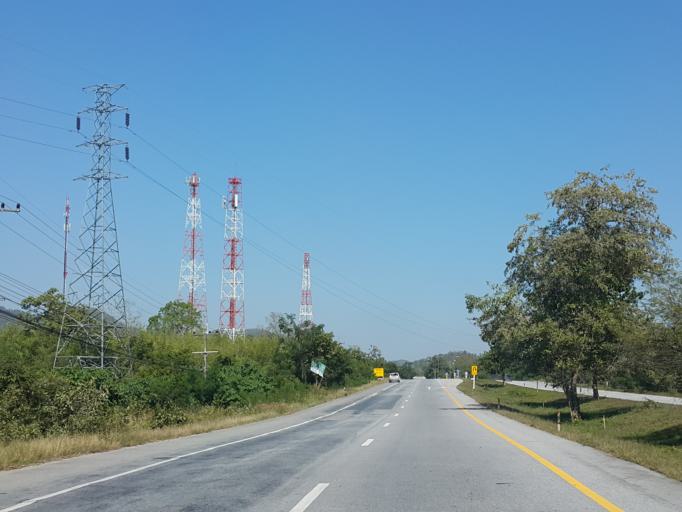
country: TH
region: Lampang
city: Sop Prap
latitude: 17.7894
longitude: 99.2621
